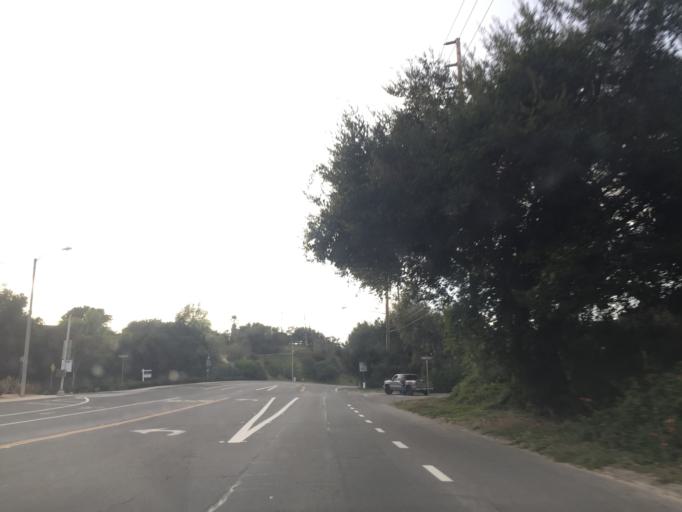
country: US
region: California
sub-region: Santa Barbara County
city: Goleta
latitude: 34.4517
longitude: -119.8026
